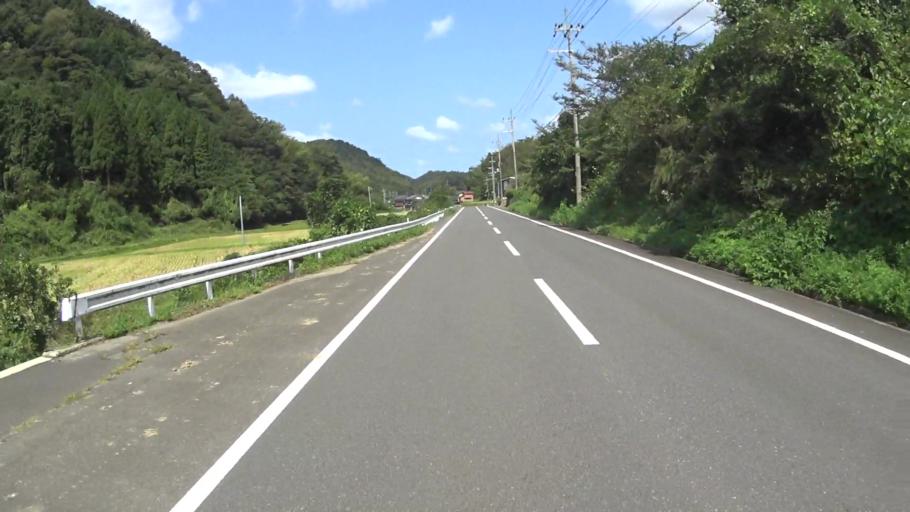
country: JP
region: Kyoto
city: Miyazu
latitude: 35.6941
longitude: 135.2508
